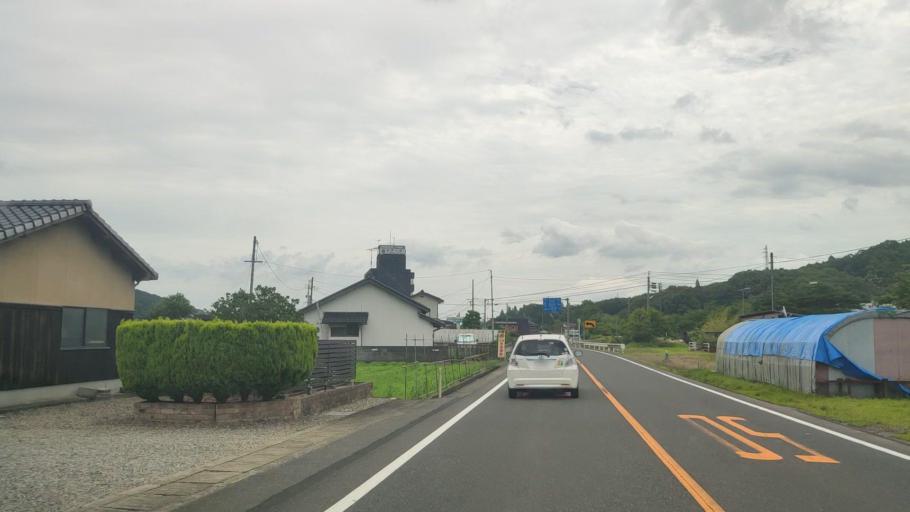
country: JP
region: Okayama
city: Tsuyama
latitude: 35.0615
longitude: 133.8727
